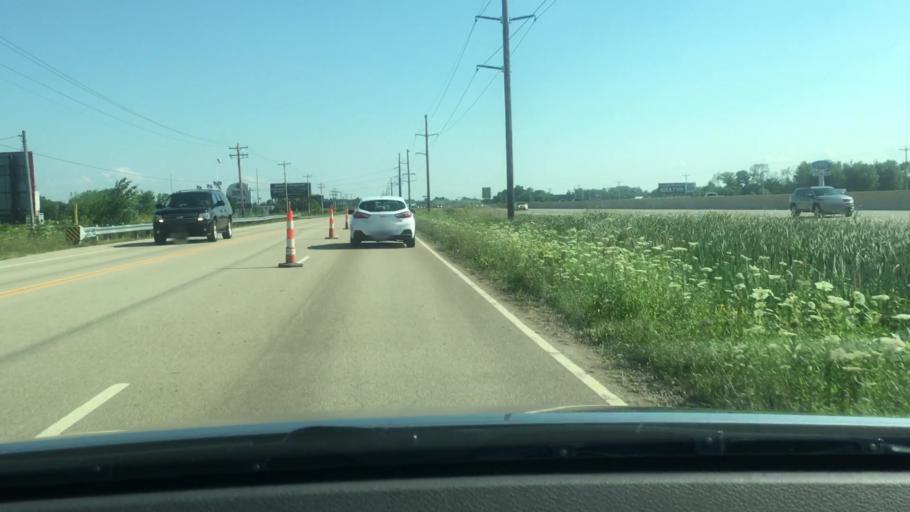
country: US
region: Wisconsin
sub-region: Winnebago County
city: Oshkosh
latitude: 43.9625
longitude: -88.5825
